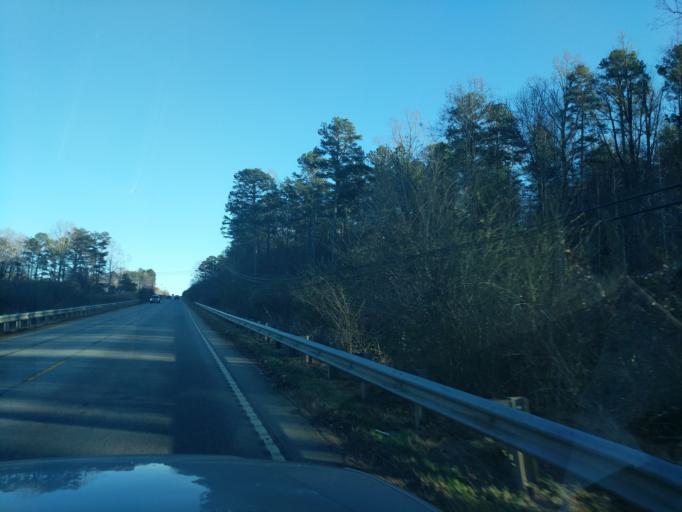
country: US
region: South Carolina
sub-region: Oconee County
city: Westminster
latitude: 34.6859
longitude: -83.1361
